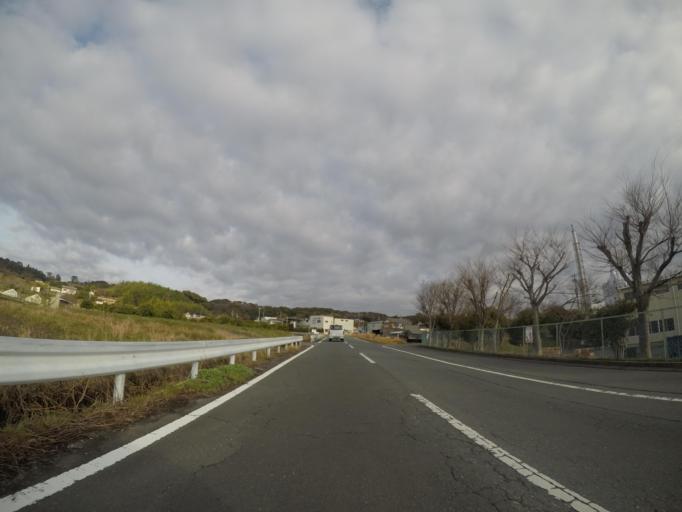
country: JP
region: Shizuoka
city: Hamakita
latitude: 34.8209
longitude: 137.7622
